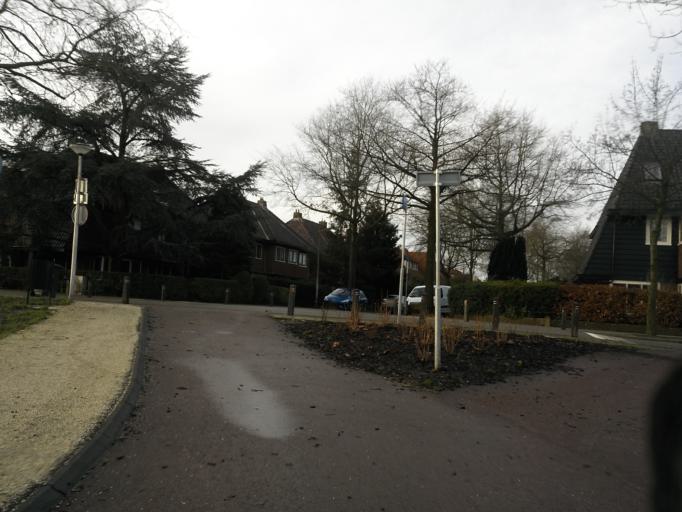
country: NL
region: Utrecht
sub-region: Gemeente Amersfoort
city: Randenbroek
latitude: 52.1481
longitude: 5.3951
